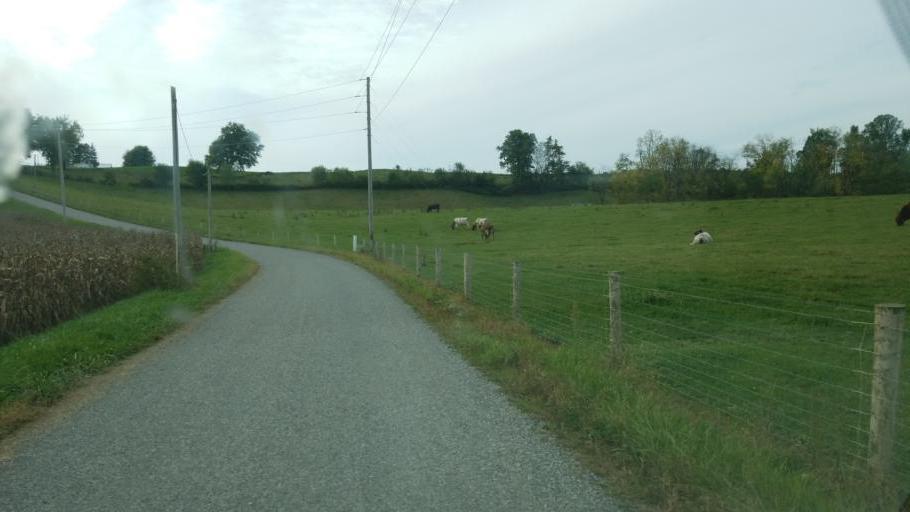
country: US
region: Ohio
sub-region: Holmes County
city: Millersburg
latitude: 40.5862
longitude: -81.8364
